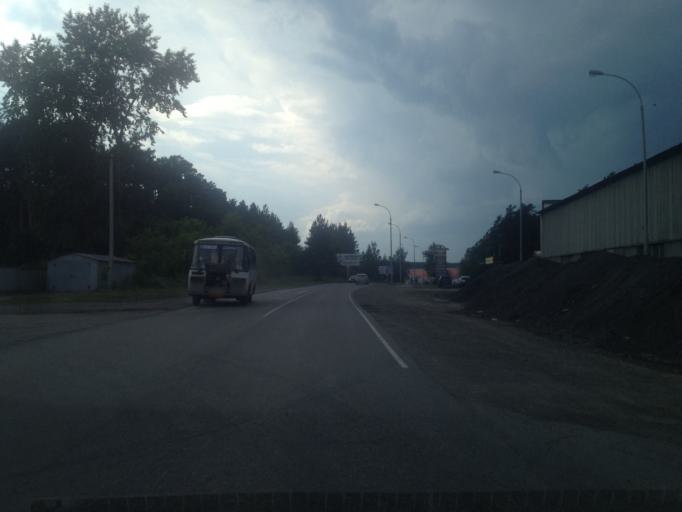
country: RU
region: Sverdlovsk
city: Shirokaya Rechka
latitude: 56.8178
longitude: 60.5128
